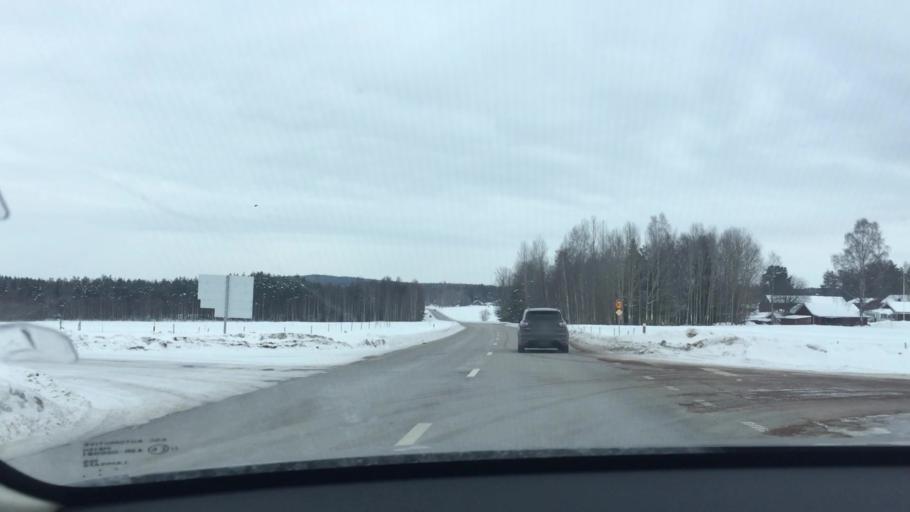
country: SE
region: Dalarna
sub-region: Faluns Kommun
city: Svardsjo
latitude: 60.6434
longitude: 15.8413
